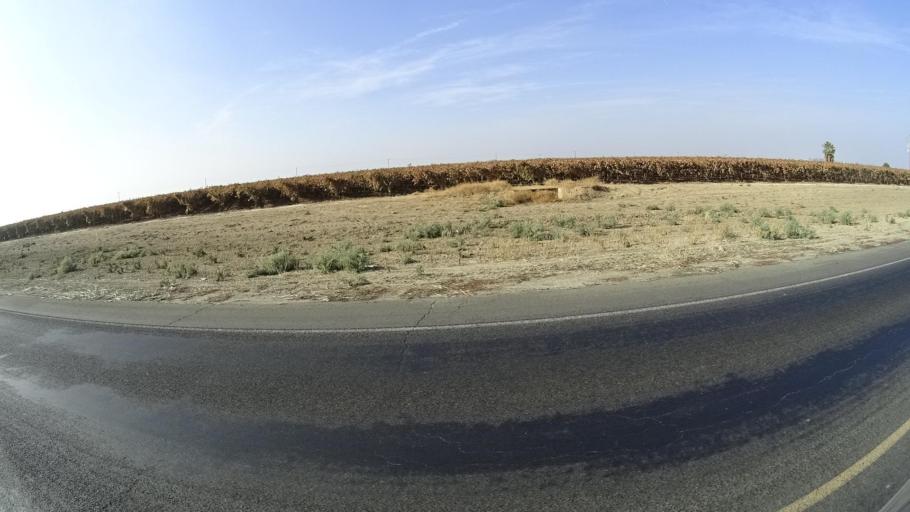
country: US
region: California
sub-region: Kern County
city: McFarland
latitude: 35.7095
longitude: -119.1651
